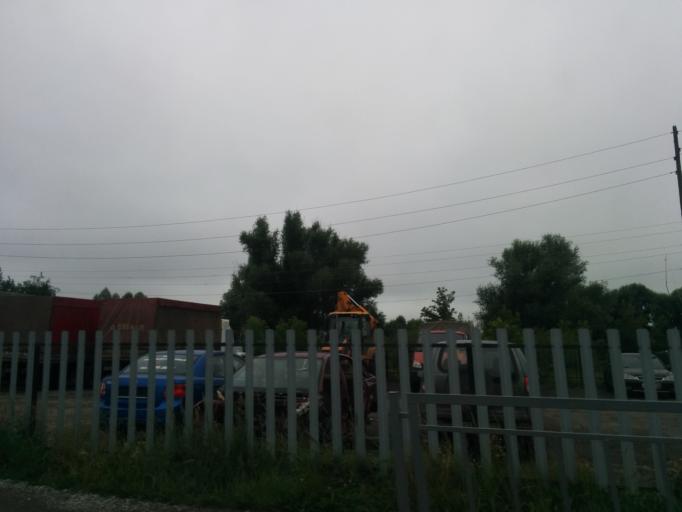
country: RU
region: Perm
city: Kondratovo
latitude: 57.9969
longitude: 56.1355
